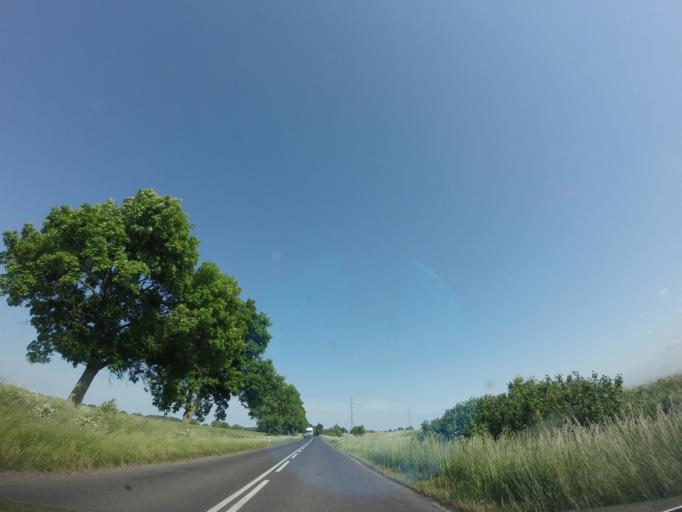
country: PL
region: West Pomeranian Voivodeship
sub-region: Powiat gryfinski
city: Stare Czarnowo
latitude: 53.3043
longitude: 14.8014
